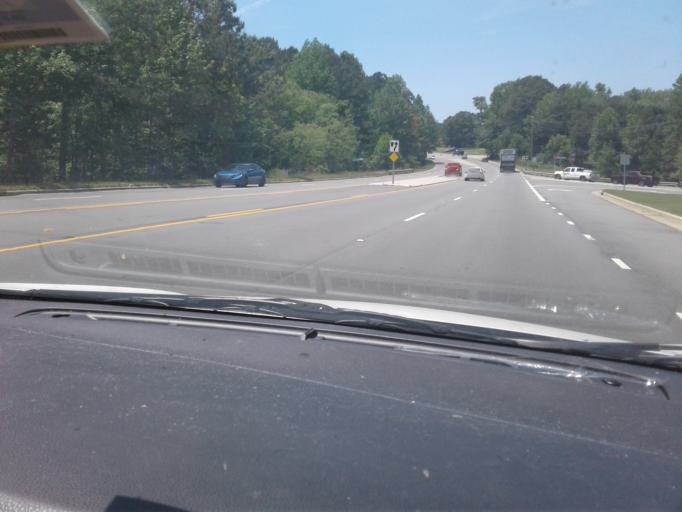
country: US
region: North Carolina
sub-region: Harnett County
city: Buies Creek
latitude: 35.4035
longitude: -78.7401
